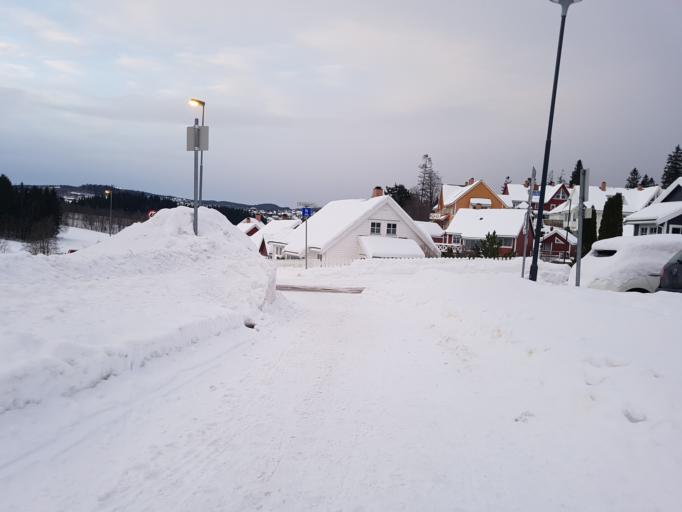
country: NO
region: Sor-Trondelag
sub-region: Trondheim
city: Trondheim
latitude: 63.3789
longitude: 10.3818
